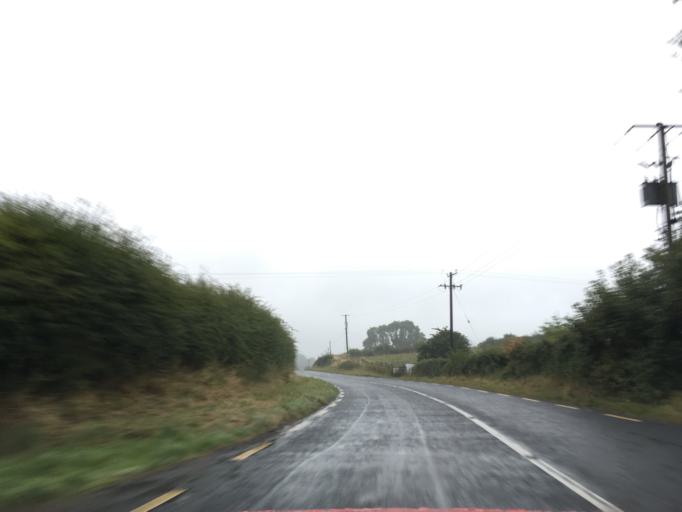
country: IE
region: Munster
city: Tipperary
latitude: 52.4777
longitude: -8.1378
